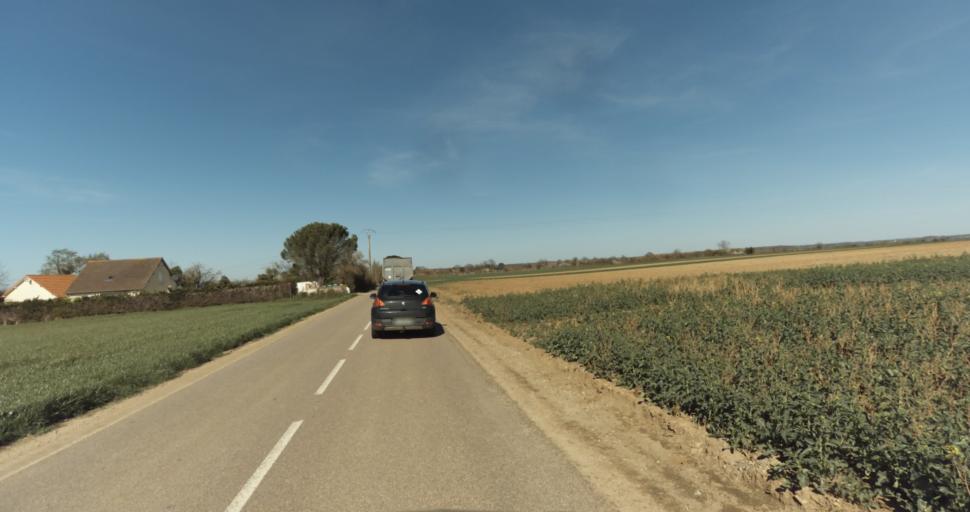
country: FR
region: Lower Normandy
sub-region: Departement du Calvados
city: Canon
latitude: 49.0472
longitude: -0.0662
